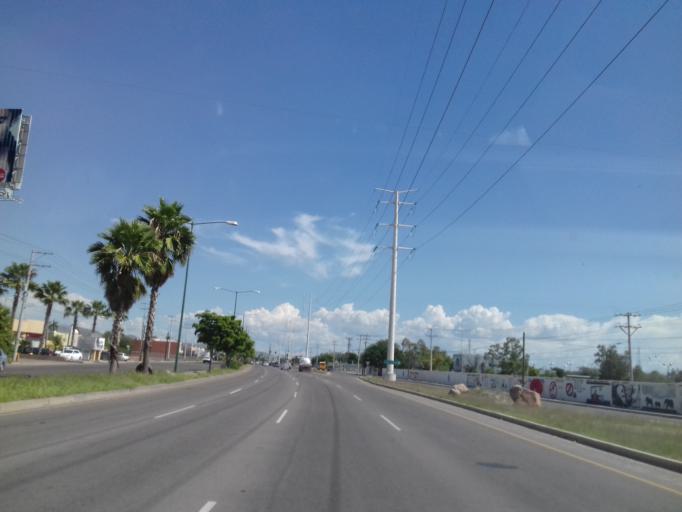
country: MX
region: Sonora
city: Hermosillo
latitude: 29.0825
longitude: -111.0043
